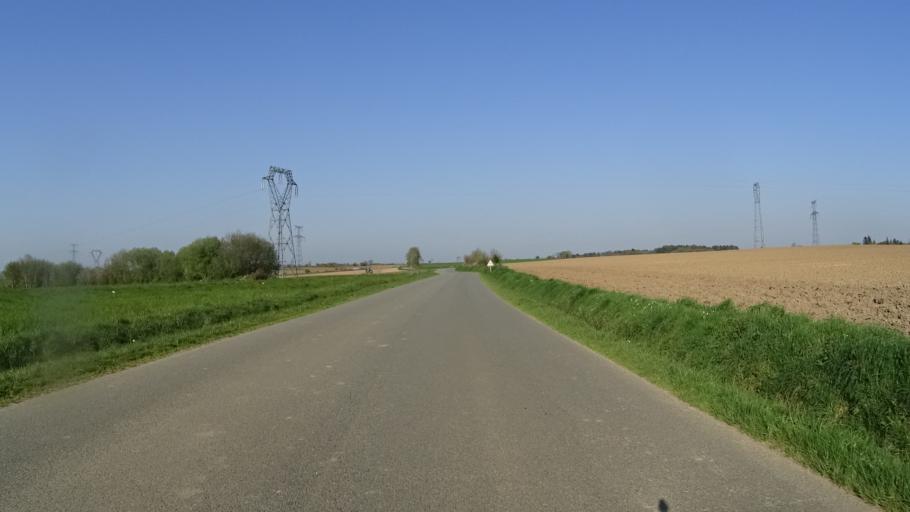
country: FR
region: Brittany
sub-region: Departement du Finistere
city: Irvillac
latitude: 48.3840
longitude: -4.1694
